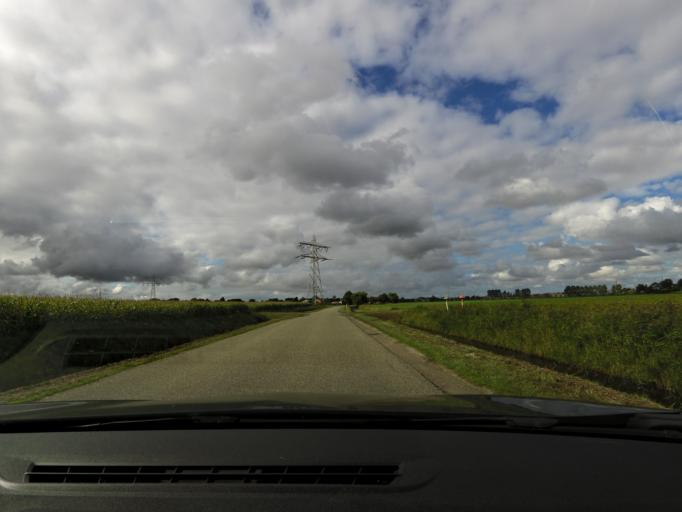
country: NL
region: South Holland
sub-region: Gemeente Brielle
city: Brielle
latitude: 51.8833
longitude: 4.1740
